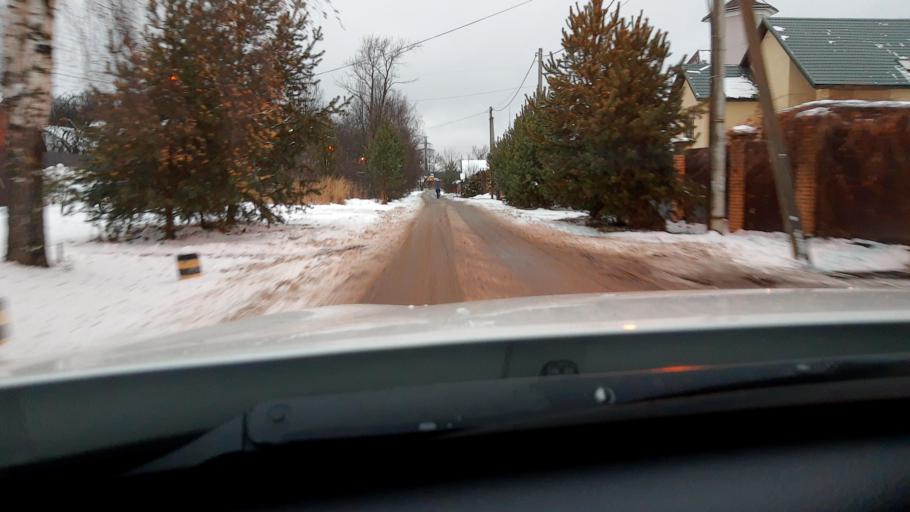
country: RU
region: Moskovskaya
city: Krasnogorsk
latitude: 55.8656
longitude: 37.3137
